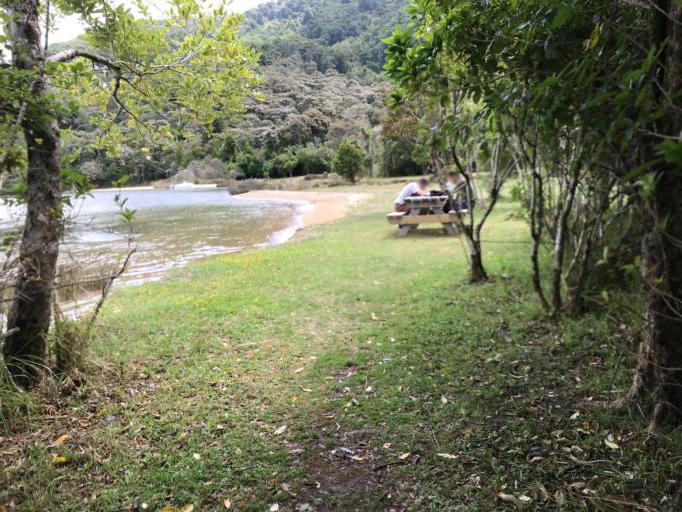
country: NZ
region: Marlborough
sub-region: Marlborough District
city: Picton
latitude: -41.2540
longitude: 173.9415
